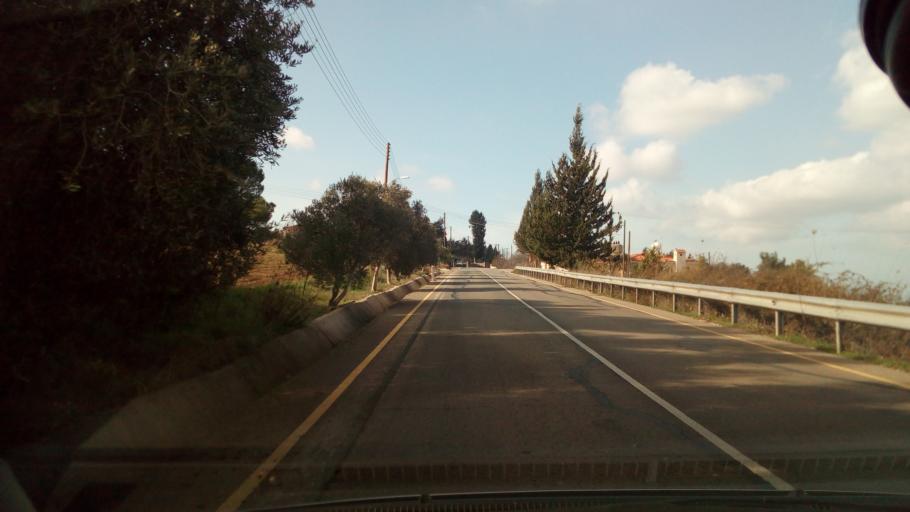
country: CY
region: Pafos
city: Polis
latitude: 34.9619
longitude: 32.4046
